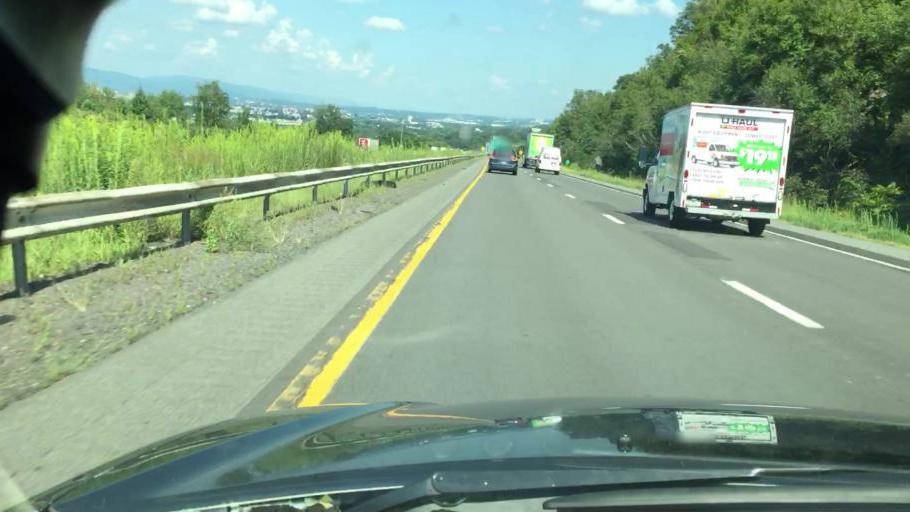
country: US
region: Pennsylvania
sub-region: Luzerne County
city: Ashley
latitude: 41.1985
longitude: -75.9097
